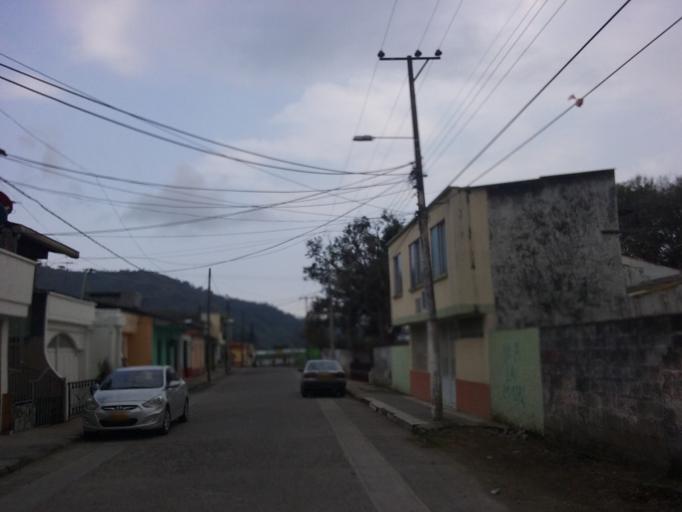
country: CO
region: Tolima
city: Libano
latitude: 4.9243
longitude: -75.0627
